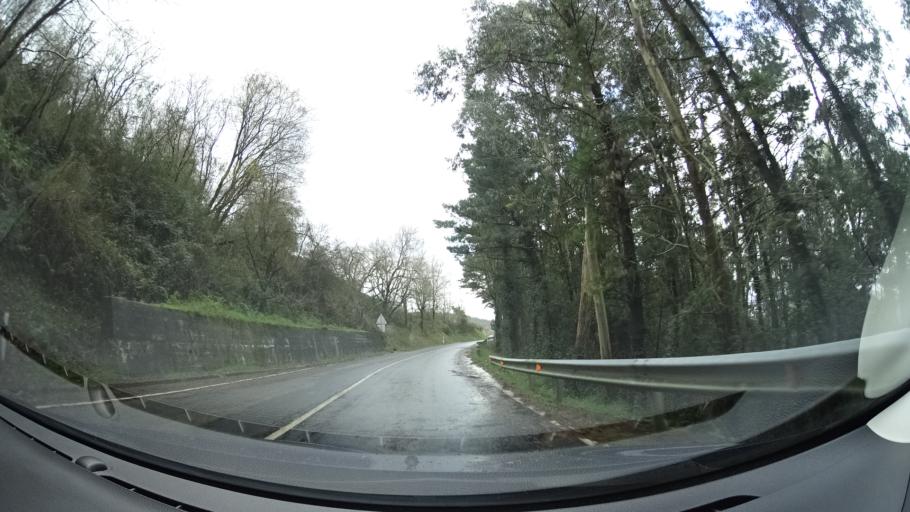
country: ES
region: Basque Country
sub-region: Bizkaia
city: Bermeo
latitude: 43.4094
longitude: -2.7556
